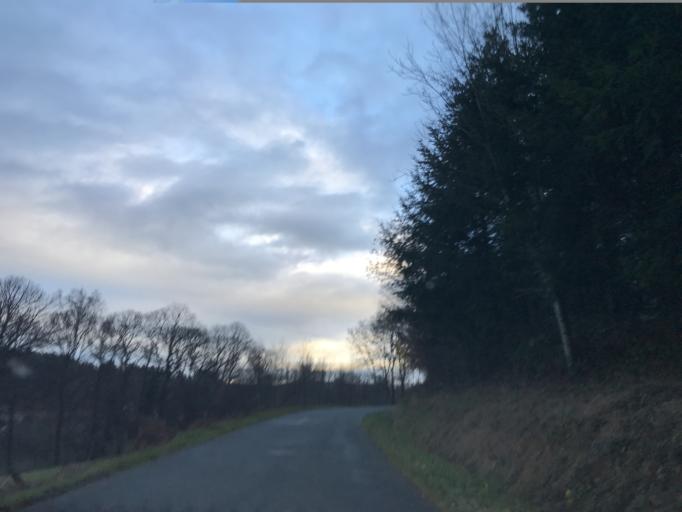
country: FR
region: Auvergne
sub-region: Departement du Puy-de-Dome
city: Celles-sur-Durolle
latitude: 45.8290
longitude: 3.6661
